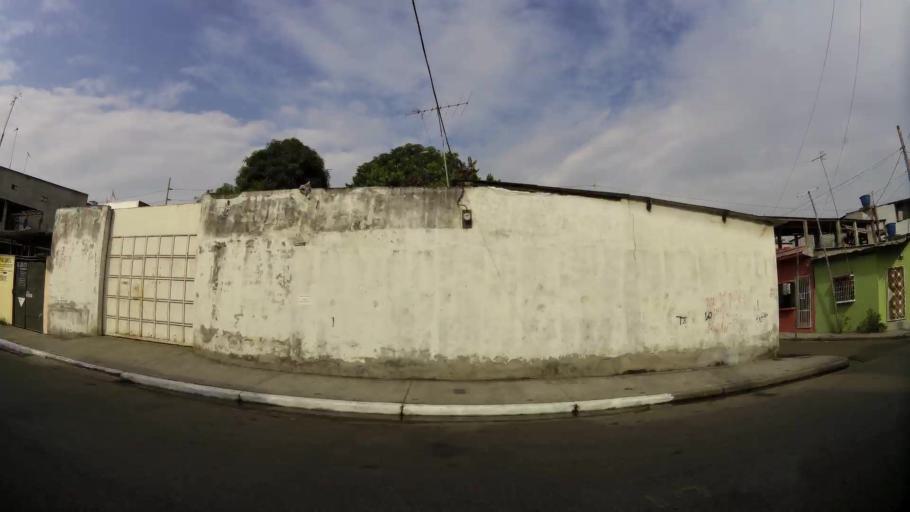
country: EC
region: Guayas
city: Guayaquil
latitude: -2.2483
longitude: -79.9049
